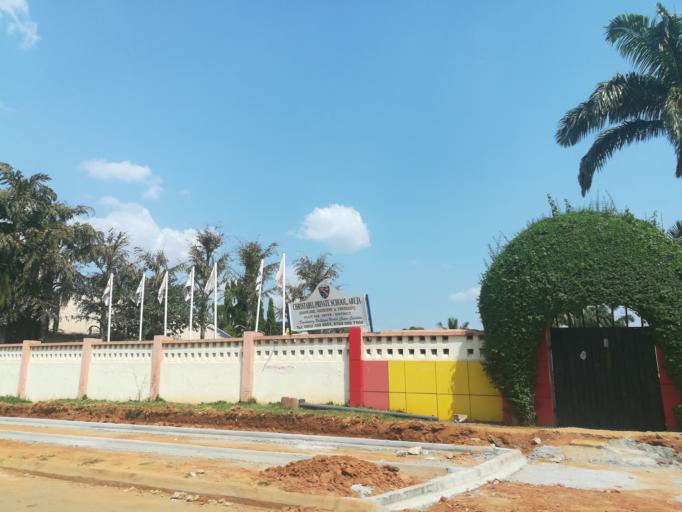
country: NG
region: Abuja Federal Capital Territory
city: Abuja
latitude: 9.0512
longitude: 7.4472
